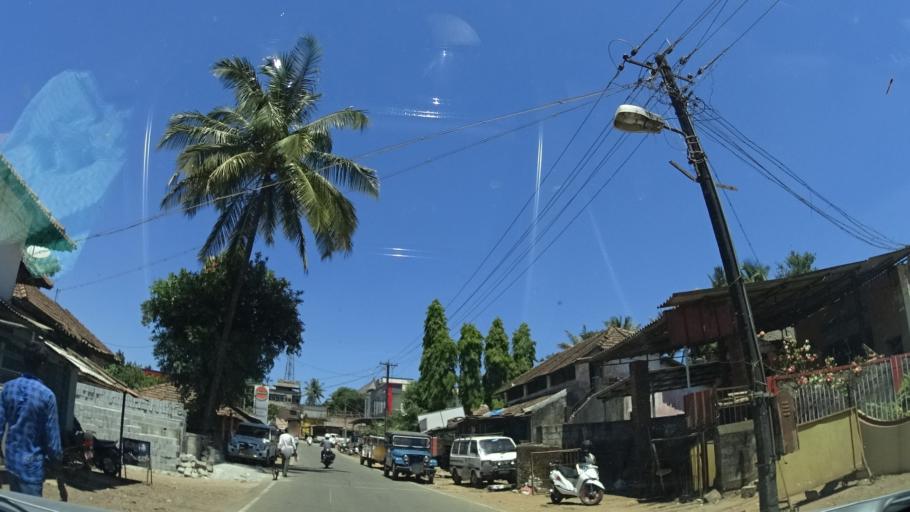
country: IN
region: Karnataka
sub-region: Chikmagalur
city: Sringeri
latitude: 13.2309
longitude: 75.3594
